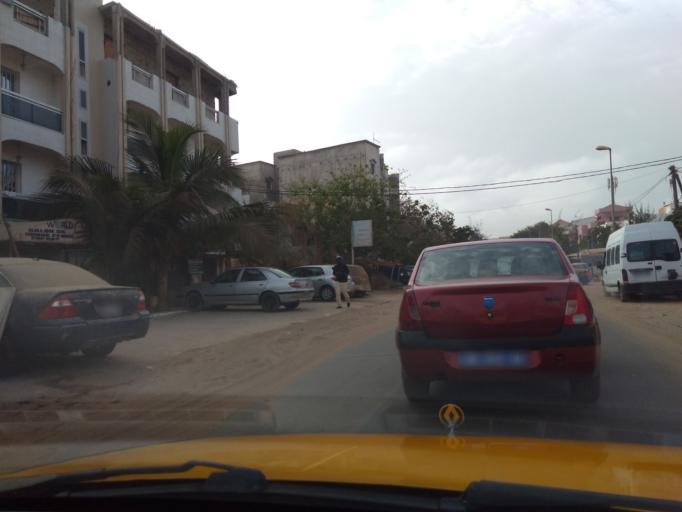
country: SN
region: Dakar
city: Grand Dakar
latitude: 14.7534
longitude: -17.4613
